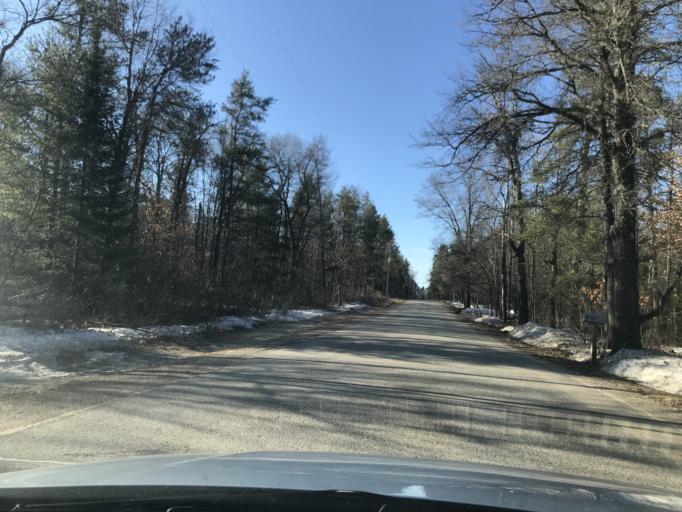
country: US
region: Michigan
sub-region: Dickinson County
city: Kingsford
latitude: 45.3925
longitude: -88.1613
